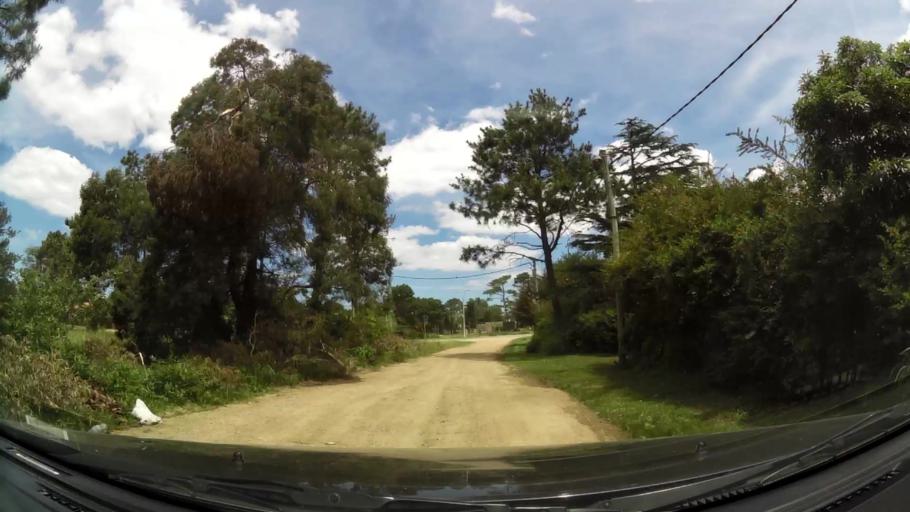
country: UY
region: Canelones
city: Pando
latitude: -34.8004
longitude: -55.8949
